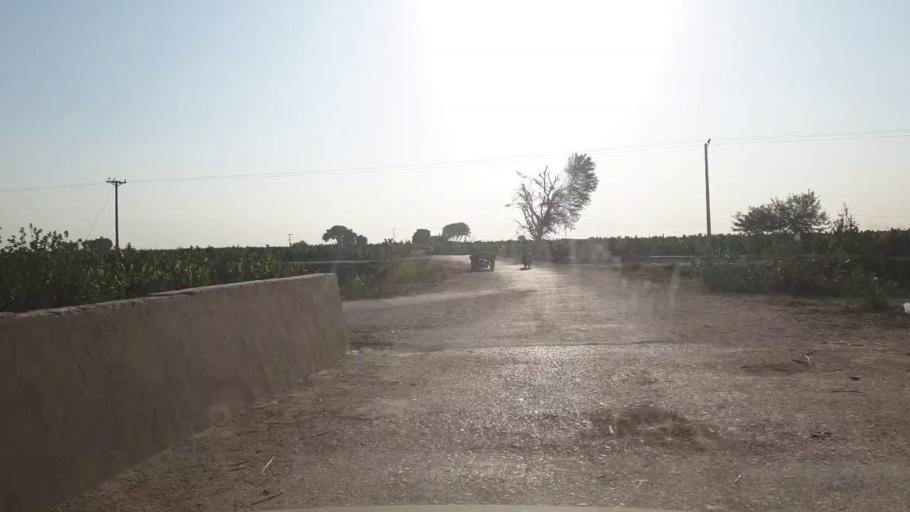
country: PK
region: Sindh
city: Tando Allahyar
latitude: 25.3623
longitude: 68.6807
